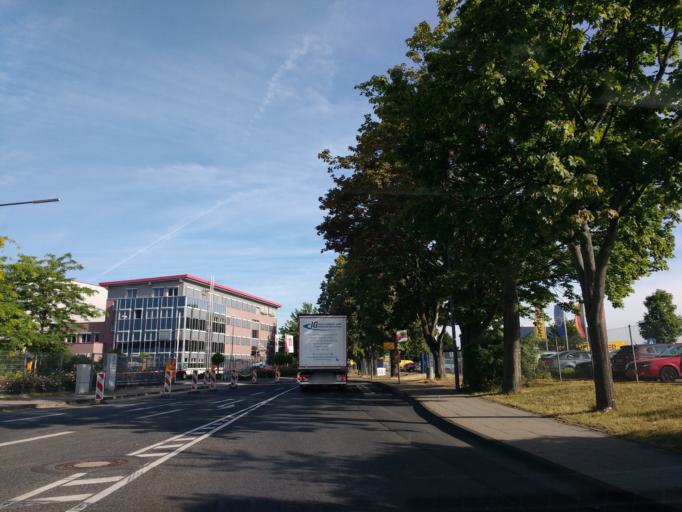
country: DE
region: North Rhine-Westphalia
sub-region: Regierungsbezirk Koln
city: Gremberghoven
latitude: 50.9100
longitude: 7.0705
